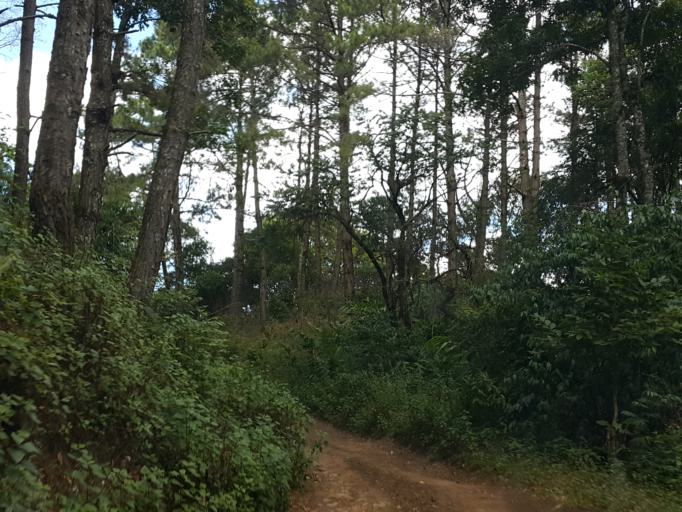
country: TH
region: Chiang Mai
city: Wiang Haeng
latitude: 19.5546
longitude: 98.8140
